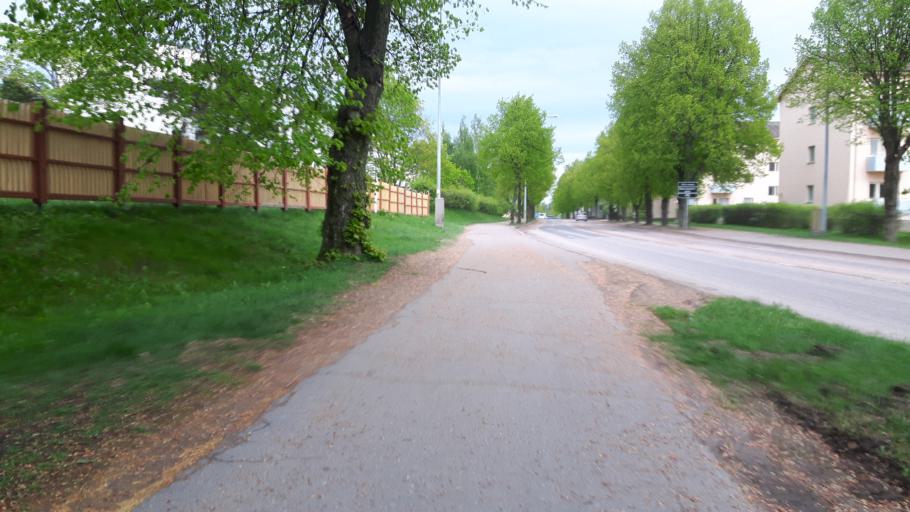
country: FI
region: Kymenlaakso
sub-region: Kotka-Hamina
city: Hamina
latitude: 60.5645
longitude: 27.2001
